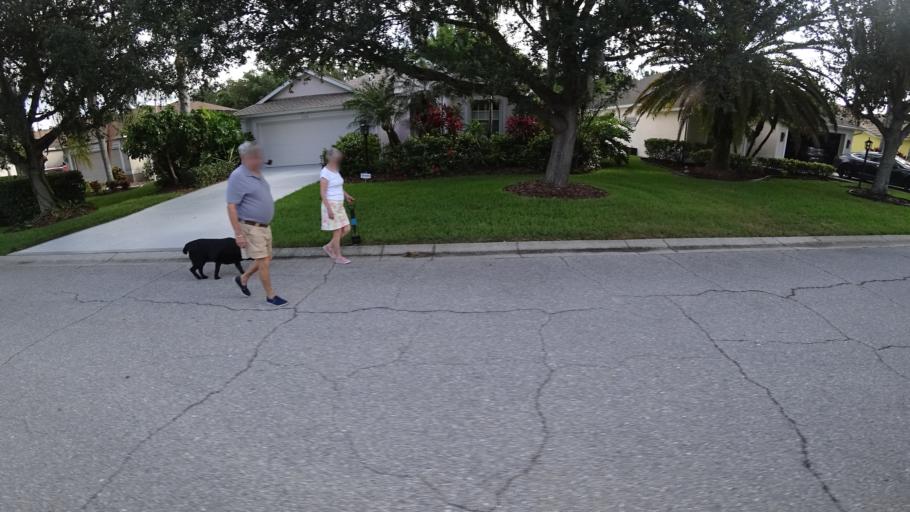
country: US
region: Florida
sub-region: Sarasota County
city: Desoto Lakes
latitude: 27.4230
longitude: -82.4941
